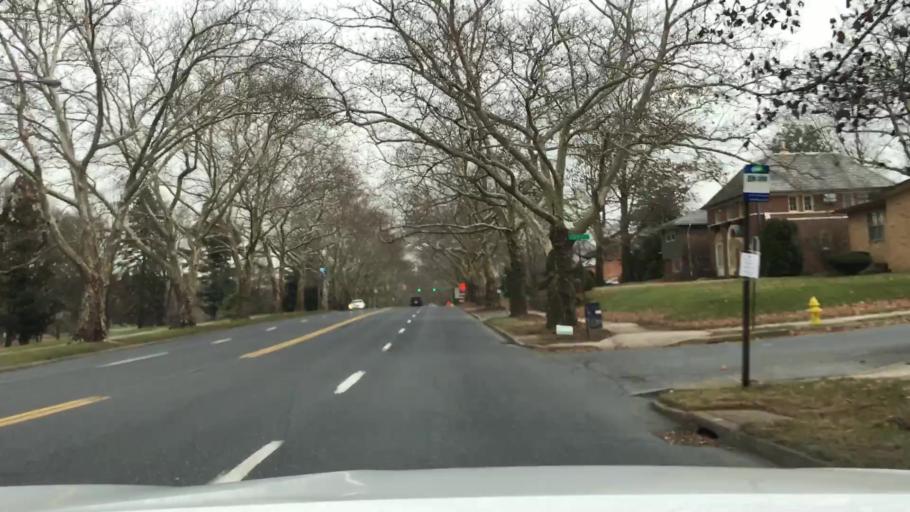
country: US
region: Pennsylvania
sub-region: Lehigh County
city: Dorneyville
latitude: 40.5919
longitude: -75.5091
